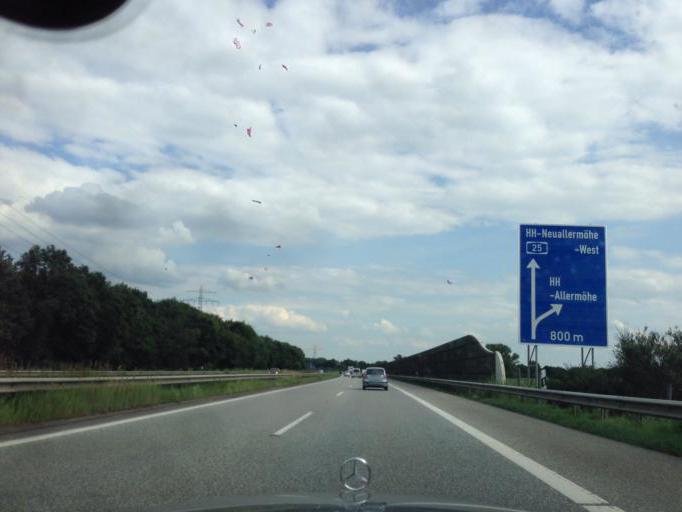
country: DE
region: Hamburg
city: Wandsbek
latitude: 53.4919
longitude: 10.1032
